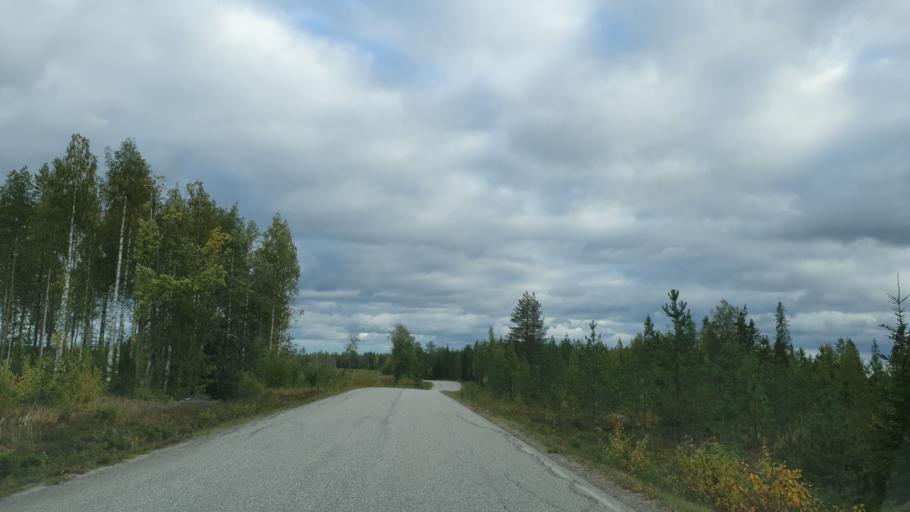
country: FI
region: Kainuu
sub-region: Kehys-Kainuu
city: Kuhmo
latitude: 63.9513
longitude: 29.7481
